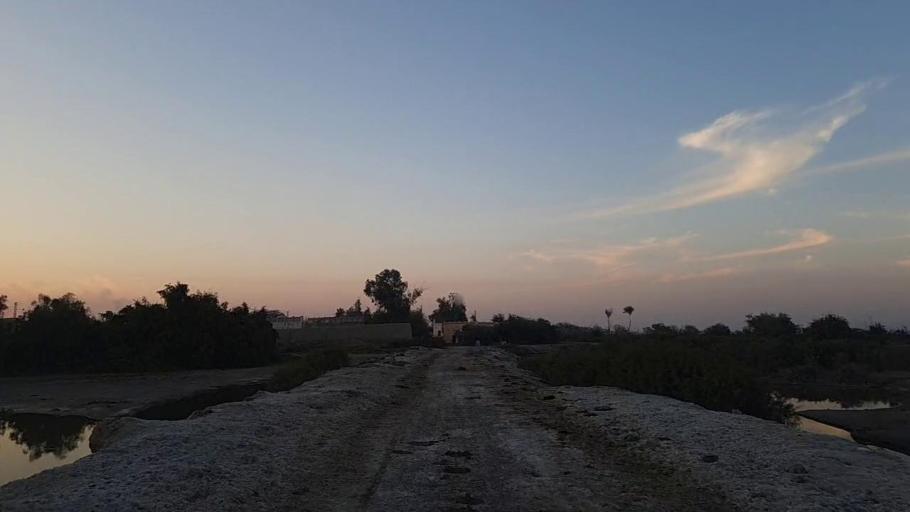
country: PK
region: Sindh
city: Bandhi
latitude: 26.5981
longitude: 68.3381
